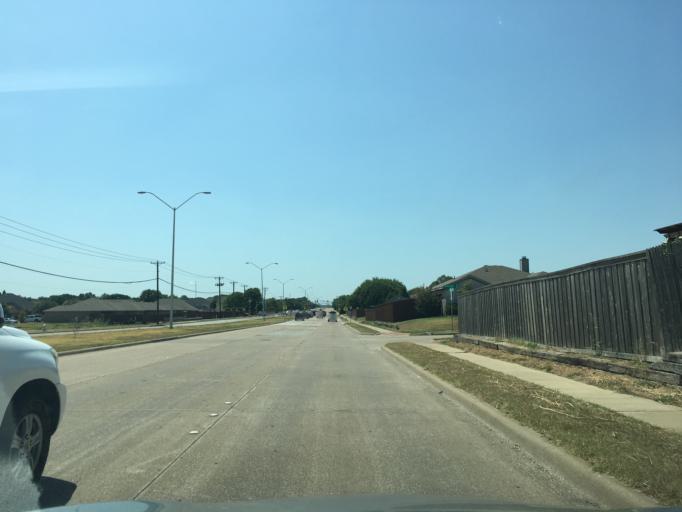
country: US
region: Texas
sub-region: Tarrant County
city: Edgecliff Village
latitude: 32.6350
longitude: -97.3550
